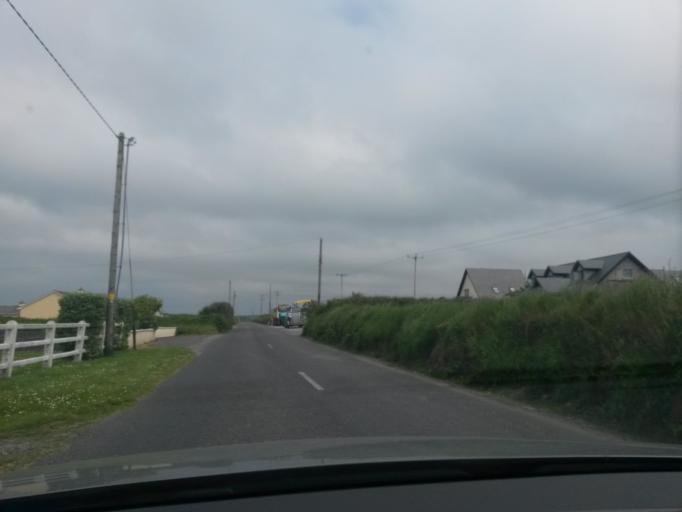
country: IE
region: Munster
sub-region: Ciarrai
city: Ballybunnion
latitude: 52.5260
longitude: -9.6656
